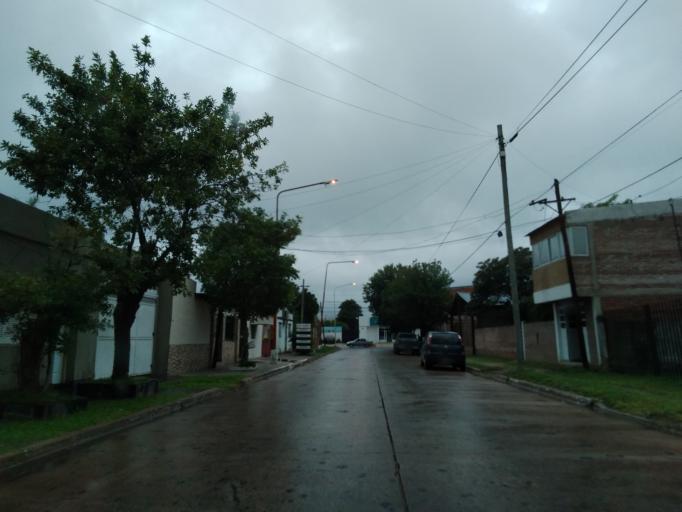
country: AR
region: Corrientes
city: Corrientes
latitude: -27.4929
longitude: -58.8209
